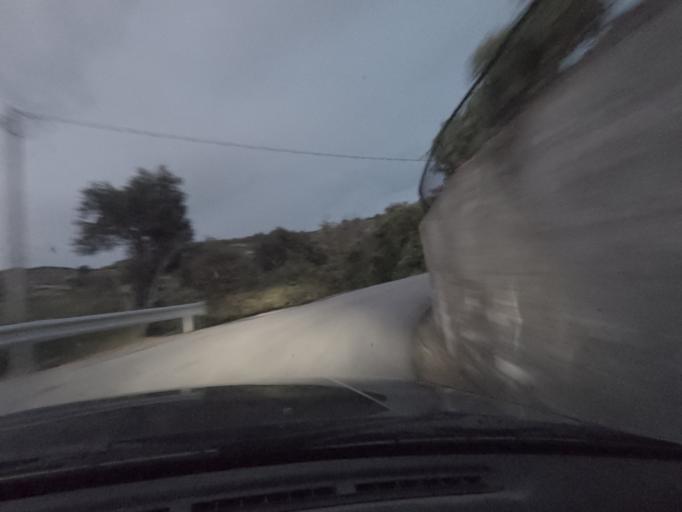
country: PT
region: Vila Real
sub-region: Peso da Regua
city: Godim
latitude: 41.1663
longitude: -7.8355
